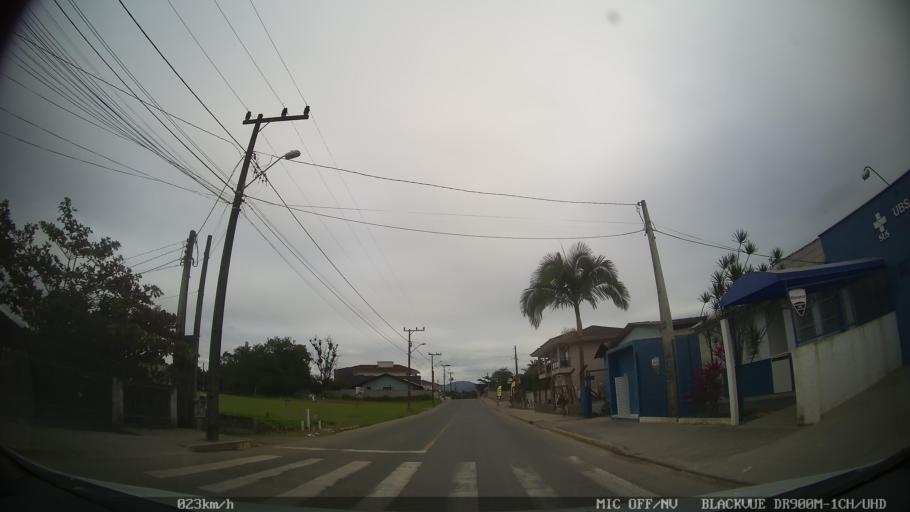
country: BR
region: Santa Catarina
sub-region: Joinville
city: Joinville
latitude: -26.3331
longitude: -48.9072
